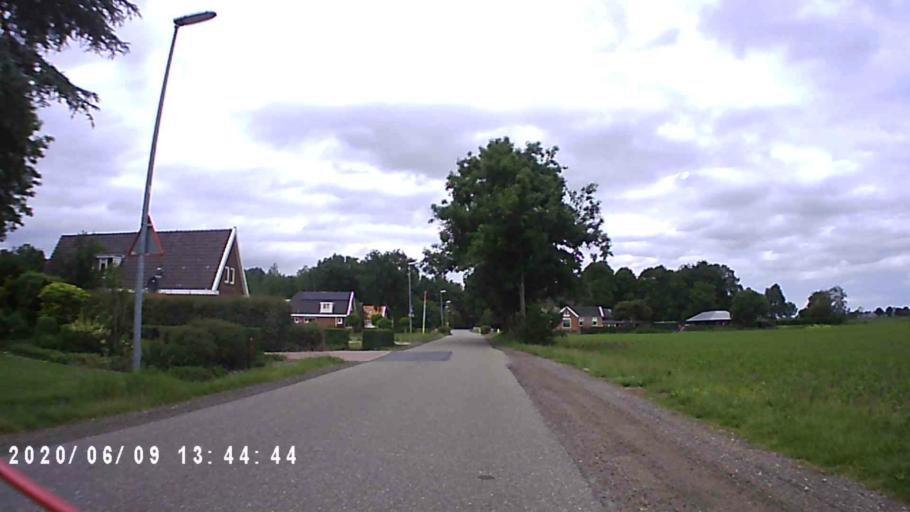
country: NL
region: Groningen
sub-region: Gemeente Groningen
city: Oosterpark
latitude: 53.2208
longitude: 6.6377
